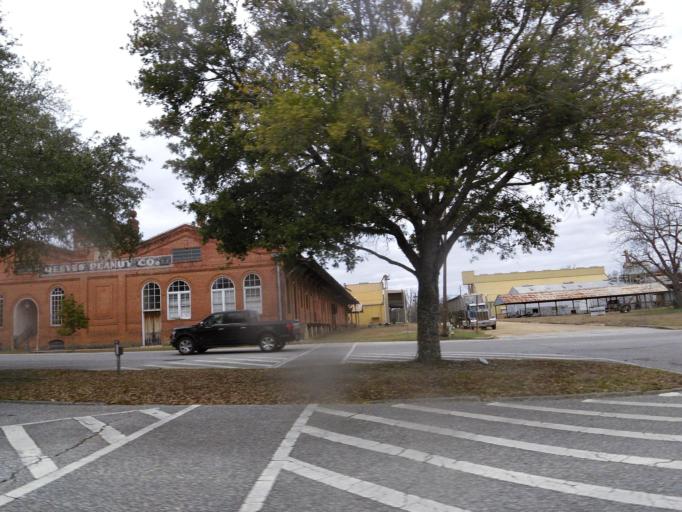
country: US
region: Alabama
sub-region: Barbour County
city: Eufaula
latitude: 31.8930
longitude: -85.1410
